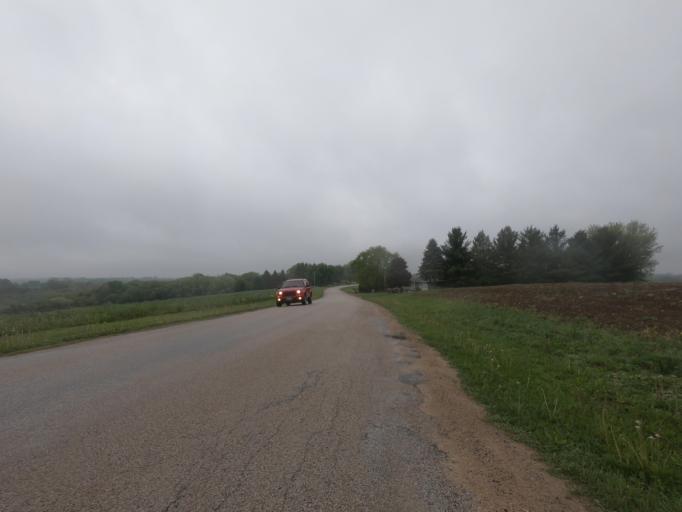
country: US
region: Wisconsin
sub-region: Grant County
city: Hazel Green
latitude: 42.4920
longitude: -90.4960
